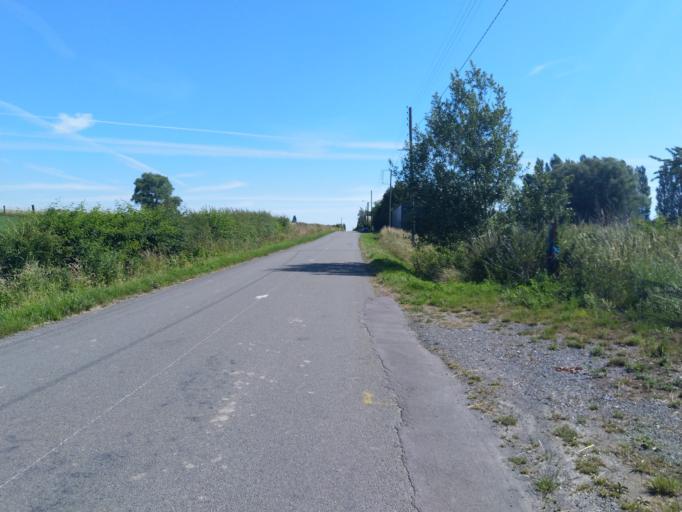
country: FR
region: Nord-Pas-de-Calais
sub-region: Departement du Nord
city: La Longueville
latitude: 50.3328
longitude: 3.8372
